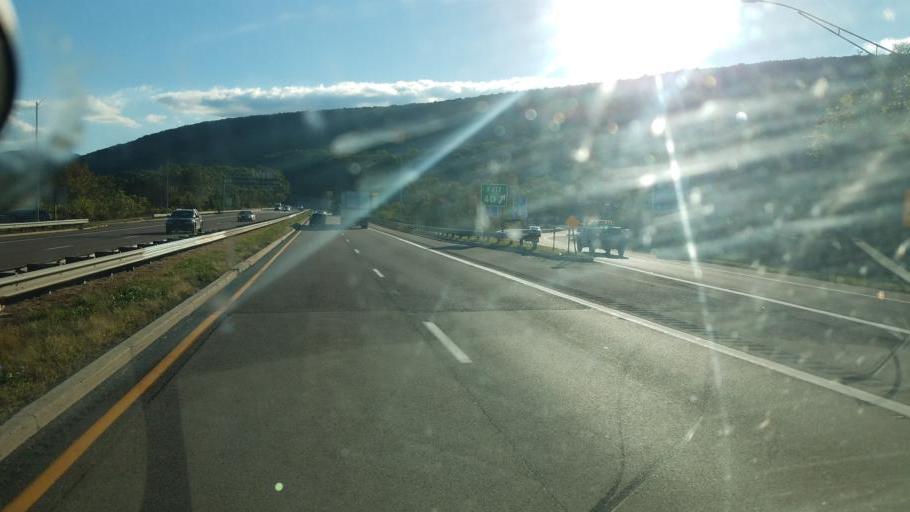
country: US
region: Maryland
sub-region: Allegany County
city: La Vale
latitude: 39.6351
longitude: -78.8315
